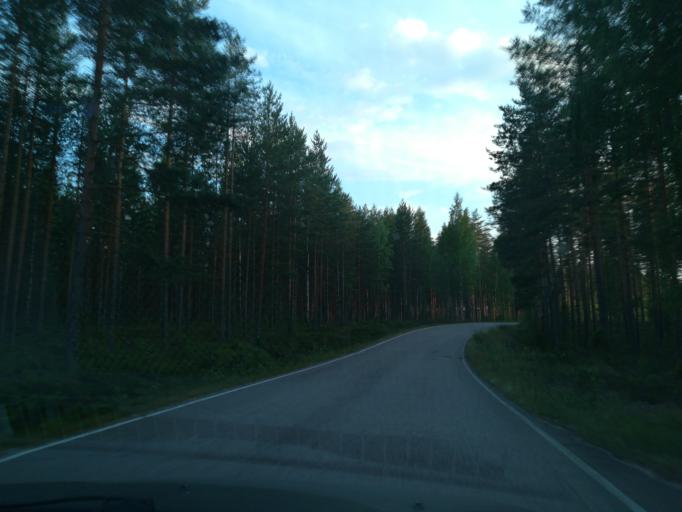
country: FI
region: South Karelia
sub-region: Lappeenranta
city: Joutseno
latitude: 61.3472
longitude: 28.4388
